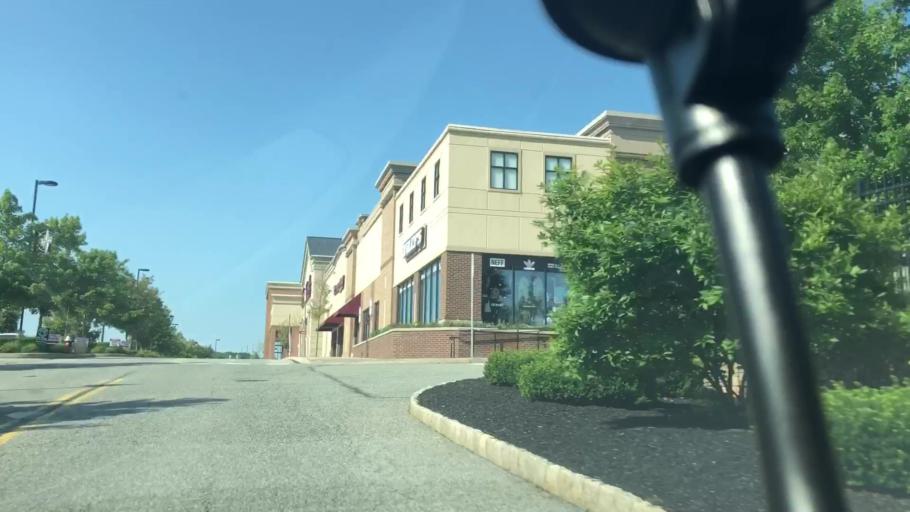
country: US
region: Pennsylvania
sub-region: Montgomery County
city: Collegeville
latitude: 40.1648
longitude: -75.4781
